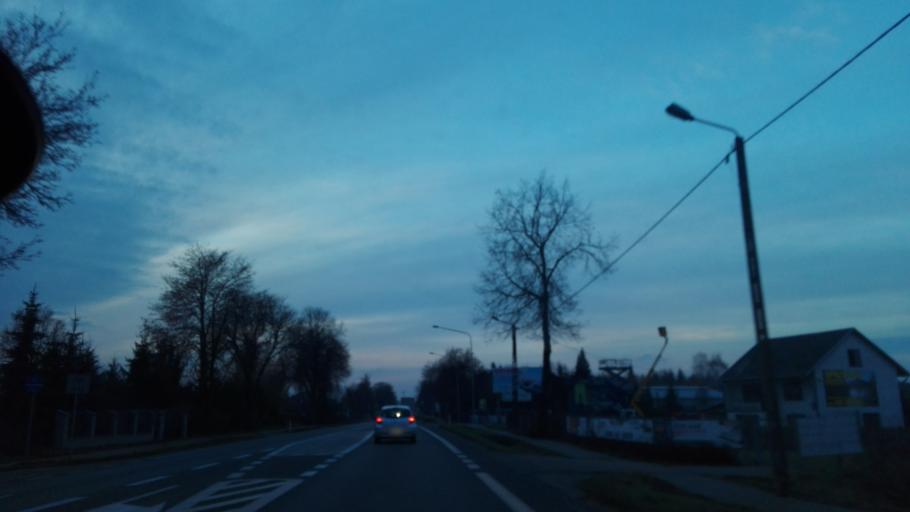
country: PL
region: Masovian Voivodeship
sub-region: Siedlce
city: Siedlce
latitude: 52.1745
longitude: 22.2022
